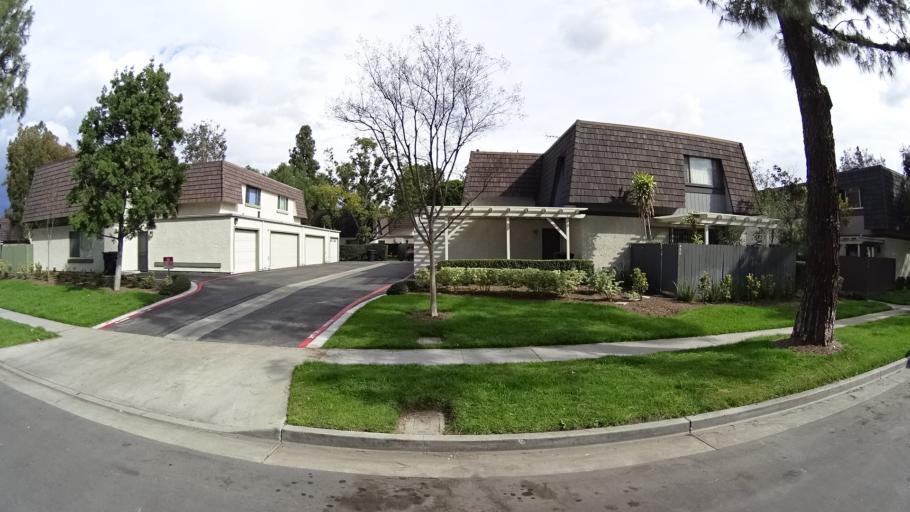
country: US
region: California
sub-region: Orange County
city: Placentia
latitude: 33.8452
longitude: -117.8692
